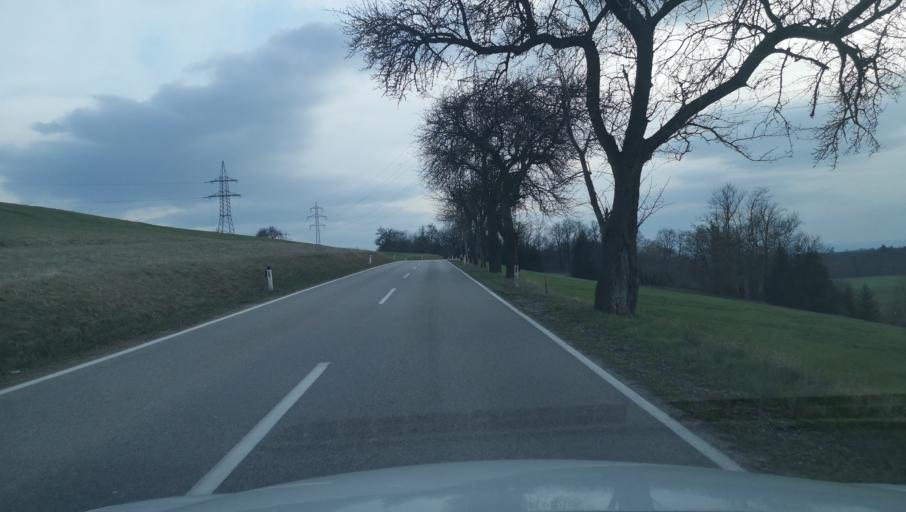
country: AT
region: Lower Austria
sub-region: Politischer Bezirk Amstetten
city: Winklarn
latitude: 48.0901
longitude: 14.8444
